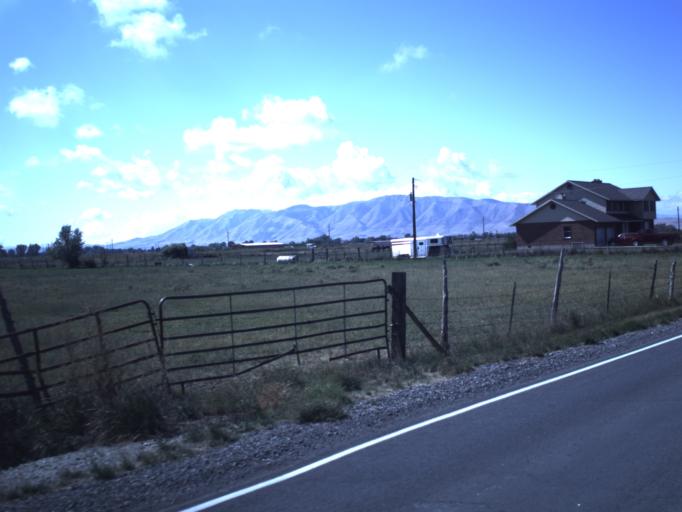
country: US
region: Utah
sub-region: Utah County
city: Spanish Fork
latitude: 40.1585
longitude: -111.6929
